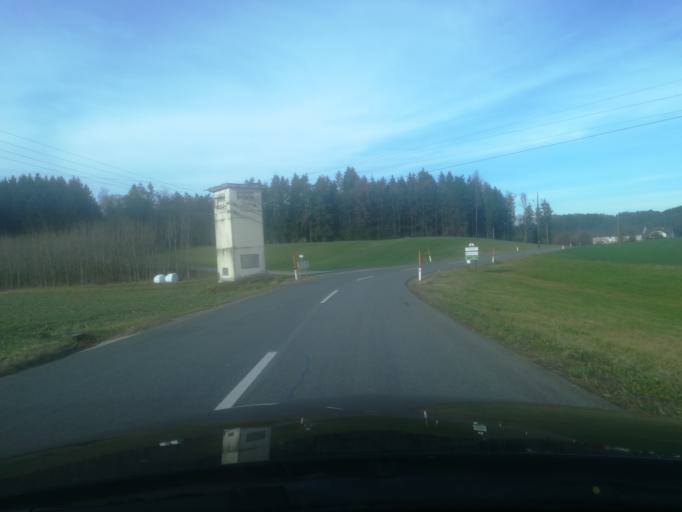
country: AT
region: Upper Austria
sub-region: Politischer Bezirk Perg
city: Perg
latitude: 48.3156
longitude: 14.6624
